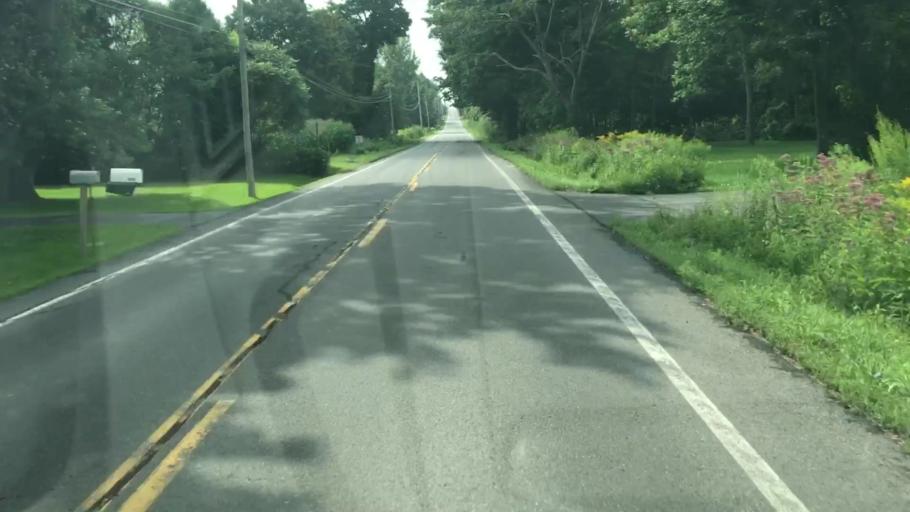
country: US
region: New York
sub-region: Onondaga County
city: Peru
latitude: 43.0517
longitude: -76.3662
